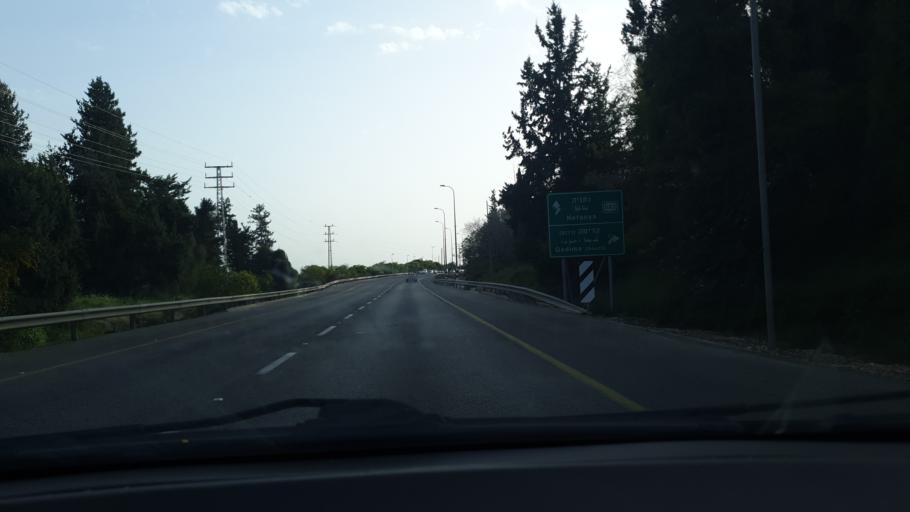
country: IL
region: Central District
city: Tel Mond
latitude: 32.2686
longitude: 34.9207
